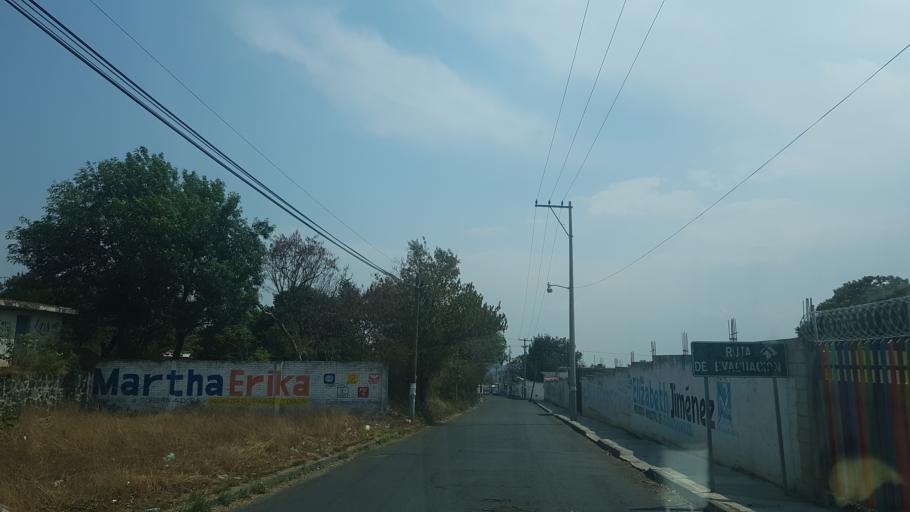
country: MX
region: Puebla
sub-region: Tianguismanalco
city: San Martin Tlapala
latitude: 18.9670
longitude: -98.4575
